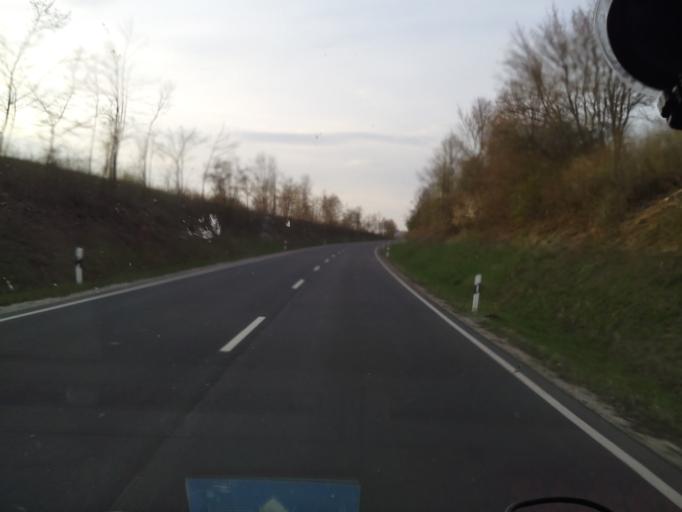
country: DE
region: Bavaria
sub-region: Regierungsbezirk Unterfranken
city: Pfarrweisach
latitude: 50.1202
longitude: 10.7634
